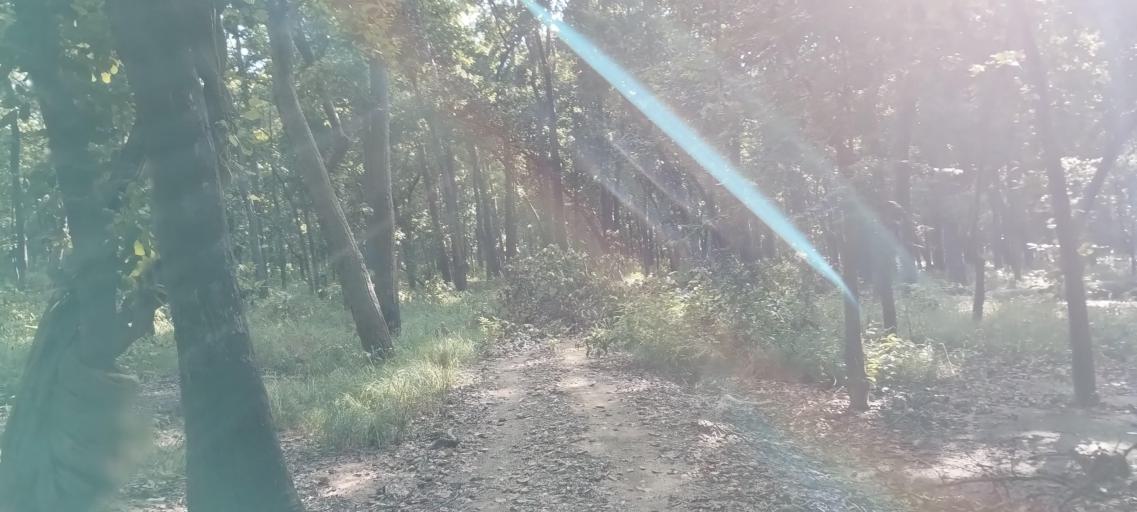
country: NP
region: Far Western
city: Tikapur
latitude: 28.5226
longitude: 81.2612
